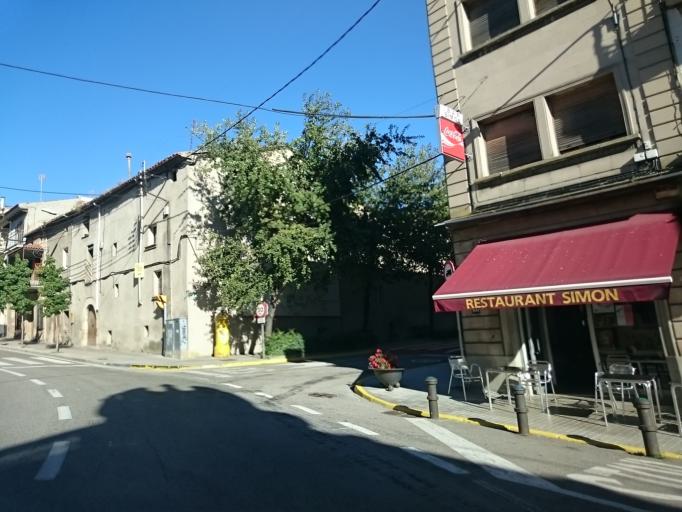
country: ES
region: Catalonia
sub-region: Provincia de Barcelona
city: Capellades
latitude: 41.5196
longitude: 1.7088
